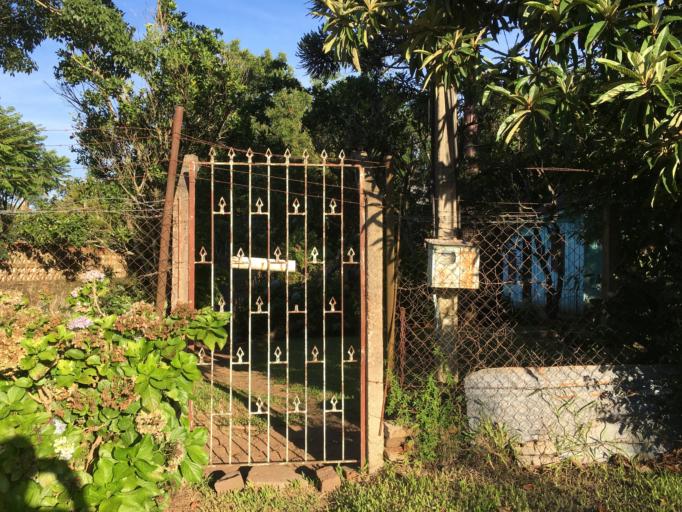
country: BR
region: Rio Grande do Sul
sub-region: Santa Maria
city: Santa Maria
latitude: -29.7004
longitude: -53.7091
